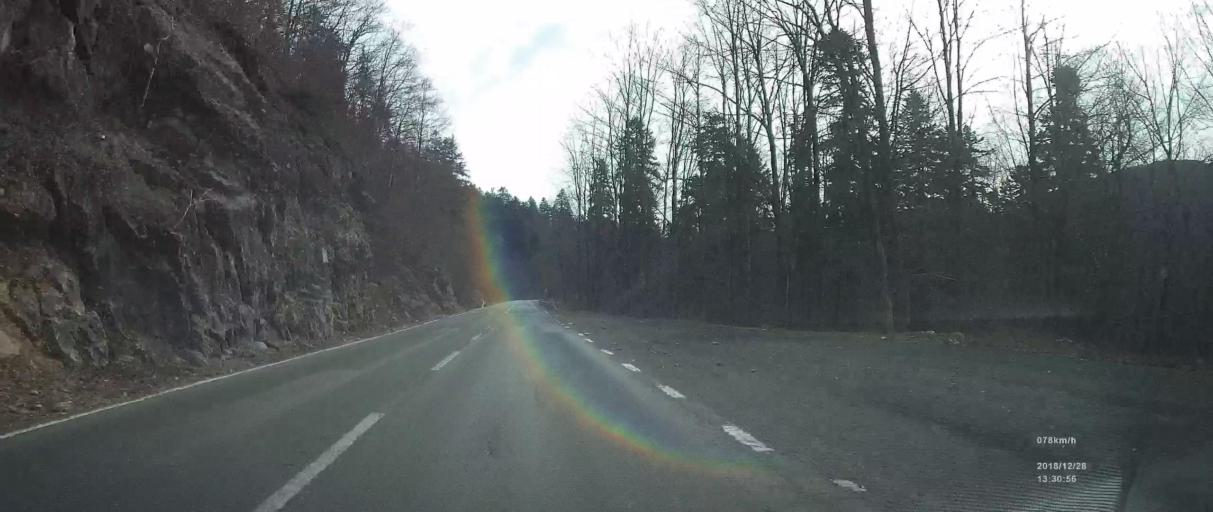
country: HR
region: Primorsko-Goranska
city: Hreljin
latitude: 45.3539
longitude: 14.6468
